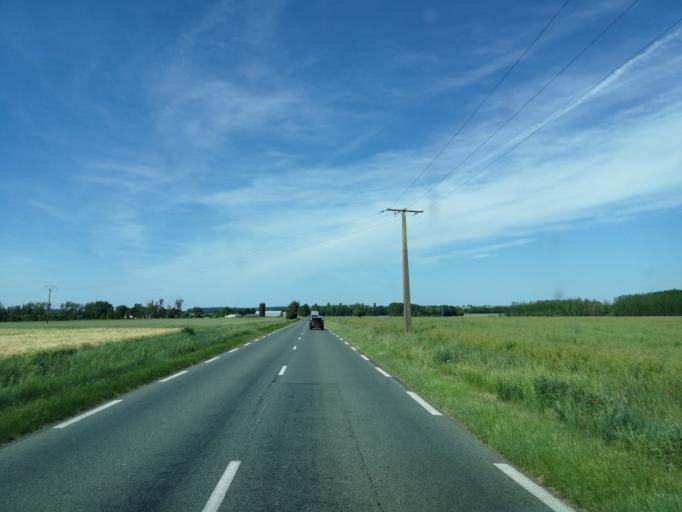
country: FR
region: Centre
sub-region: Departement d'Indre-et-Loire
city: Ligre
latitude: 47.0802
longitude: 0.1758
